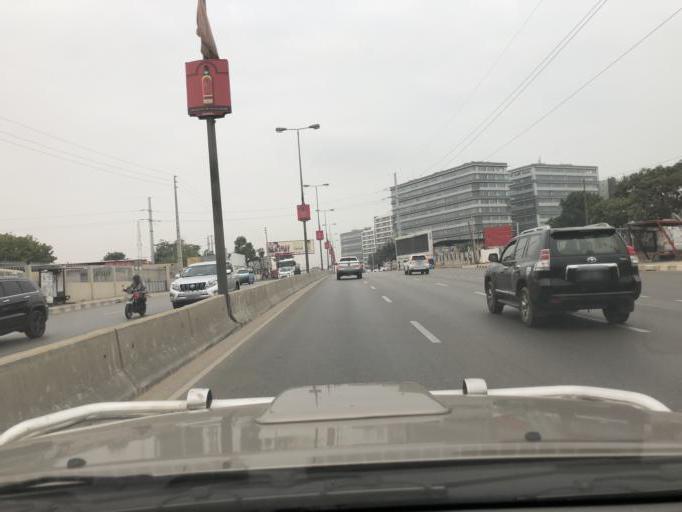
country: AO
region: Luanda
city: Luanda
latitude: -8.8846
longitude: 13.1836
